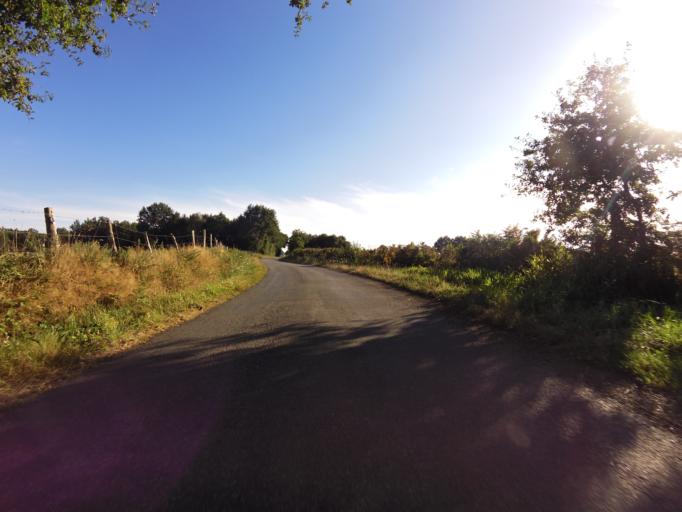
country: FR
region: Brittany
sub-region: Departement du Morbihan
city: Pluherlin
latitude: 47.7274
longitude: -2.3493
